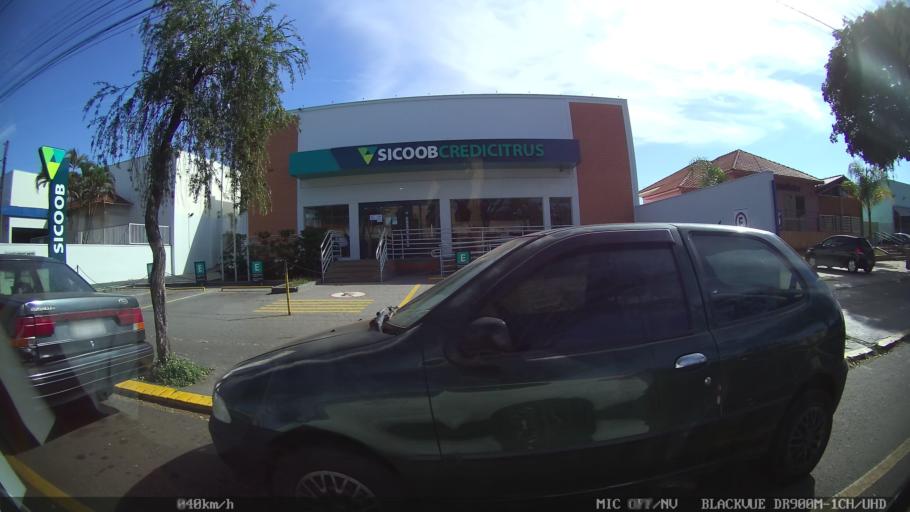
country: BR
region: Sao Paulo
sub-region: Franca
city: Franca
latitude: -20.5330
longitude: -47.4132
